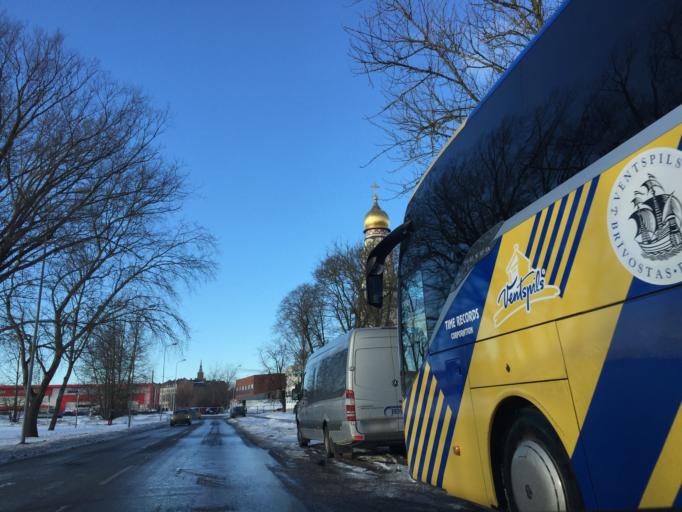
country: LV
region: Riga
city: Riga
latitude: 56.9367
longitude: 24.1407
